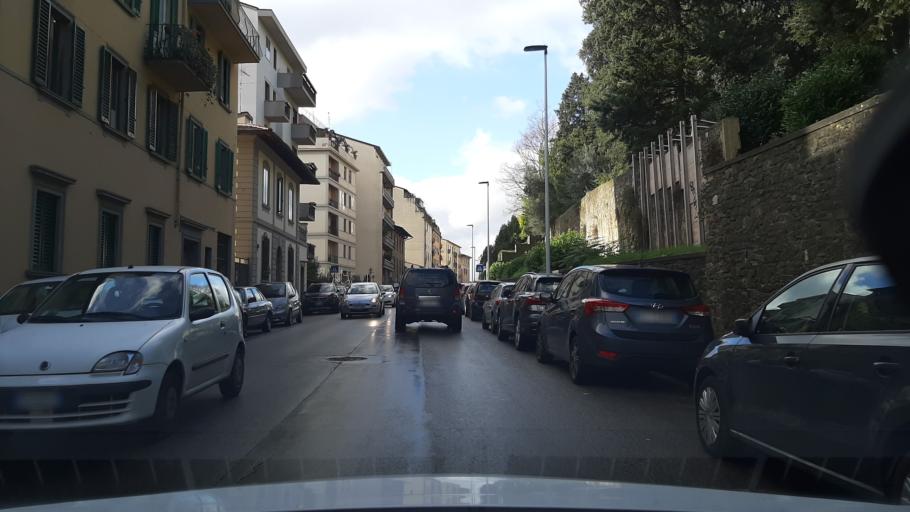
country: IT
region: Tuscany
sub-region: Province of Florence
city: Florence
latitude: 43.7931
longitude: 11.2490
